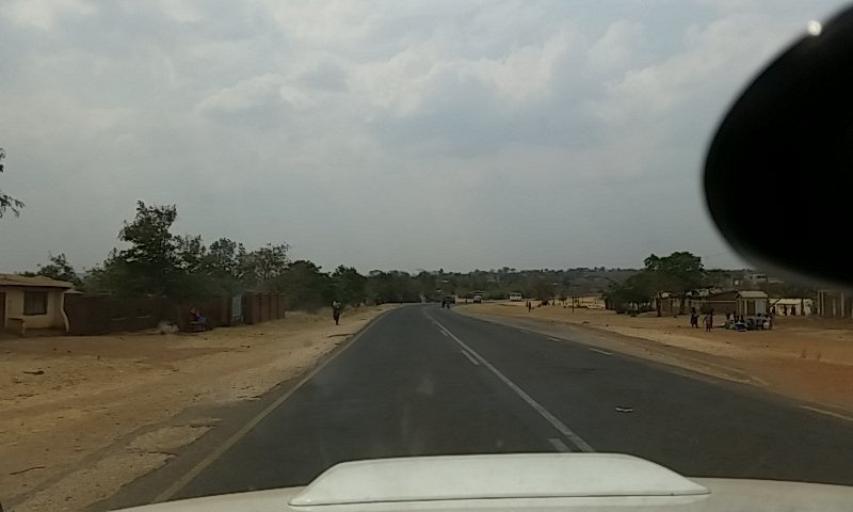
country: MW
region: Central Region
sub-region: Lilongwe District
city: Lilongwe
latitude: -13.8571
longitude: 33.8325
